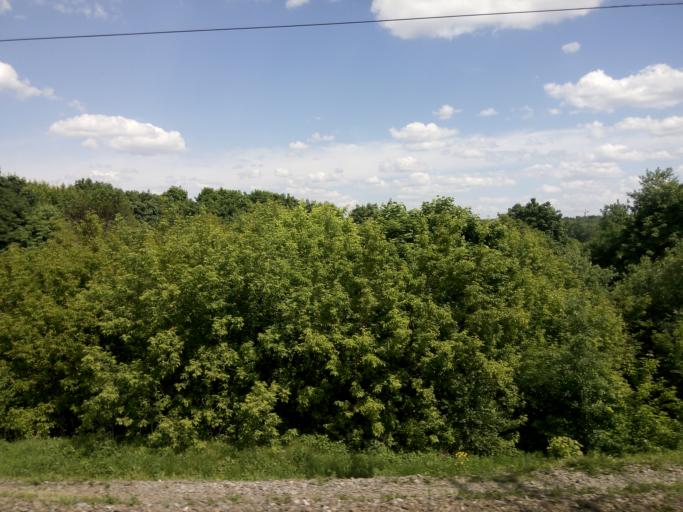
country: RU
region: Moscow
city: Zagor'ye
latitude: 55.5694
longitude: 37.6652
